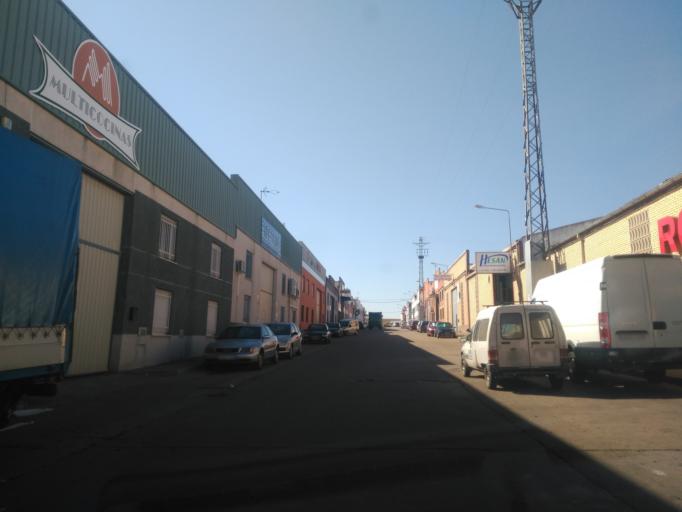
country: ES
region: Castille and Leon
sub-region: Provincia de Salamanca
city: Villares de la Reina
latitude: 40.9923
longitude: -5.6386
